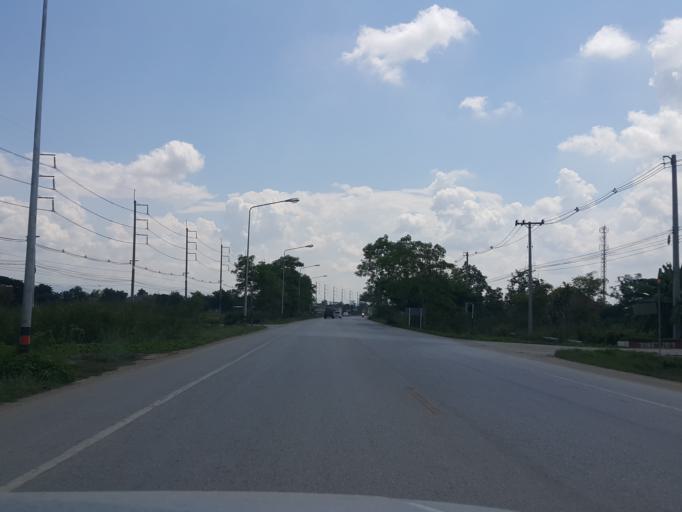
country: TH
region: Chiang Mai
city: San Sai
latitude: 18.7946
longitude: 99.0669
